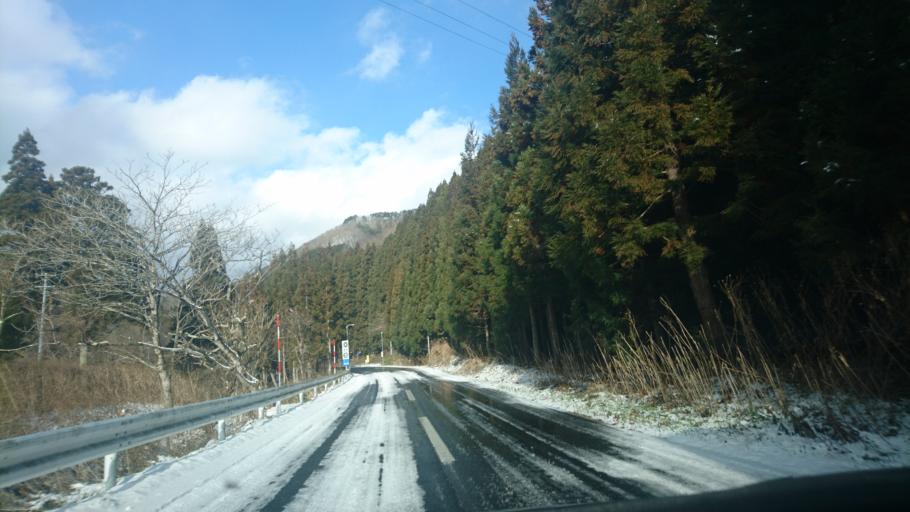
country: JP
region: Iwate
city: Tono
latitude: 39.1637
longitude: 141.3659
